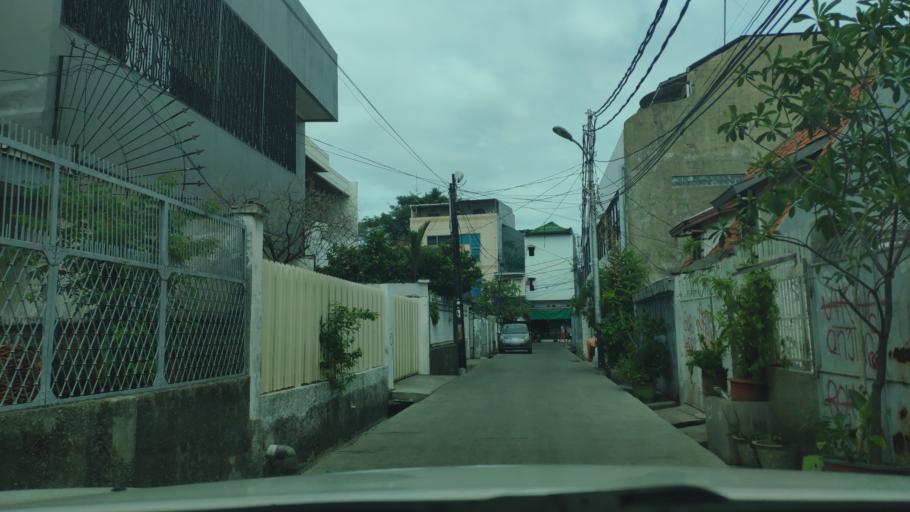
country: ID
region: Jakarta Raya
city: Jakarta
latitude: -6.1488
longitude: 106.8188
